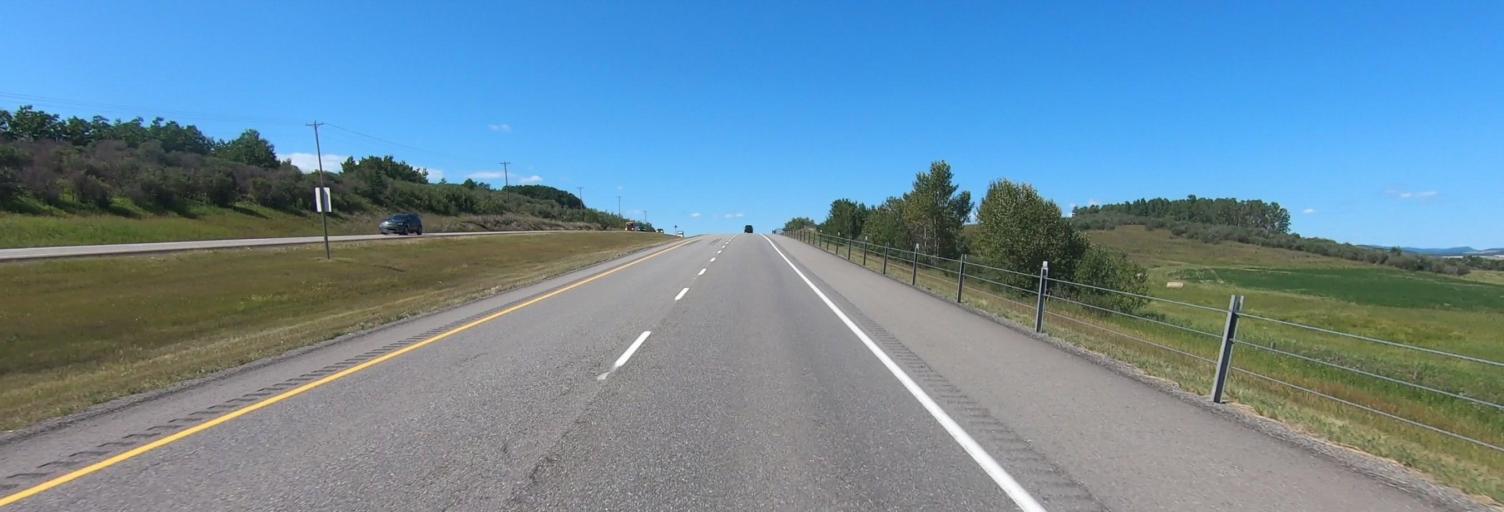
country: CA
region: Alberta
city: Cochrane
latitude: 51.0957
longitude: -114.5932
